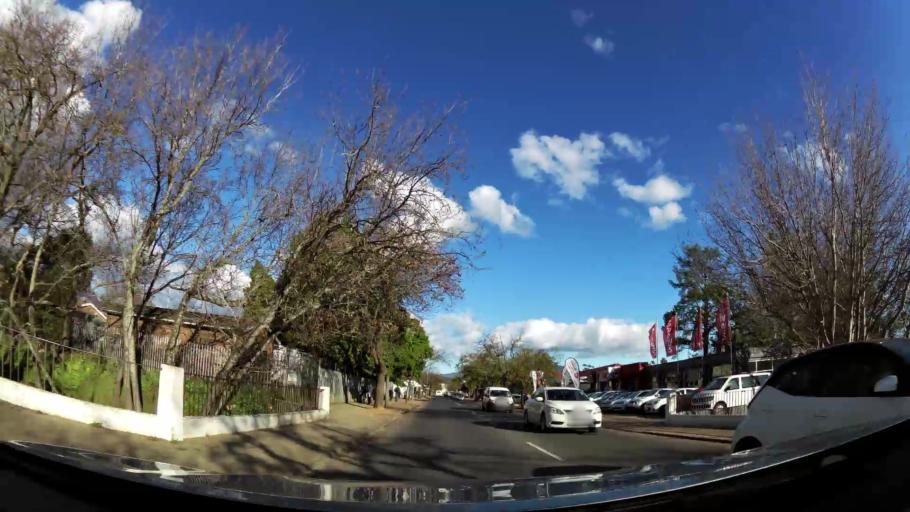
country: ZA
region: Western Cape
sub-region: Cape Winelands District Municipality
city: Stellenbosch
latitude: -33.9275
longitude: 18.8567
